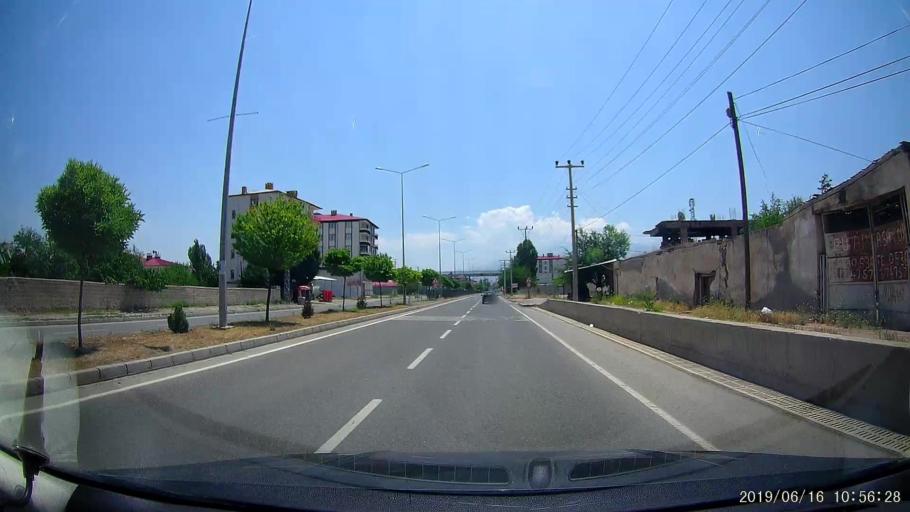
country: TR
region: Igdir
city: Igdir
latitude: 39.9294
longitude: 44.0230
